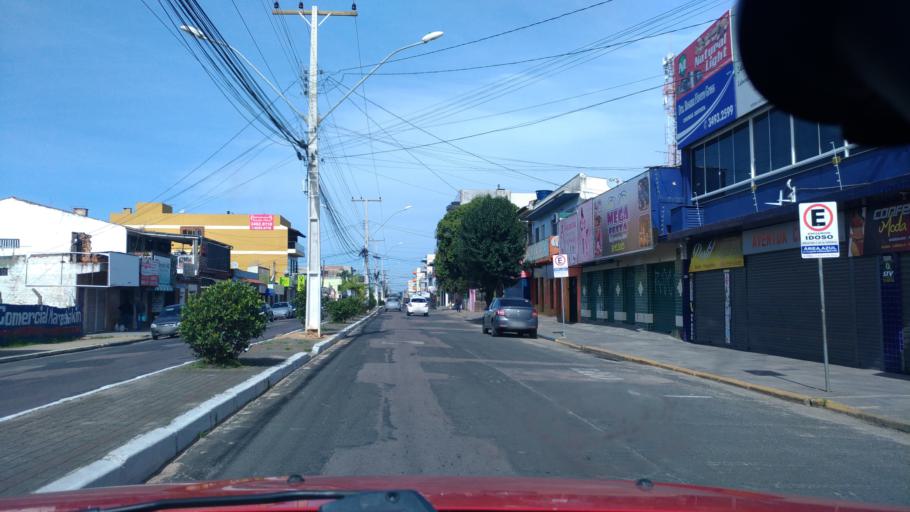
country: BR
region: Rio Grande do Sul
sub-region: Viamao
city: Viamao
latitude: -30.0626
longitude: -51.1081
